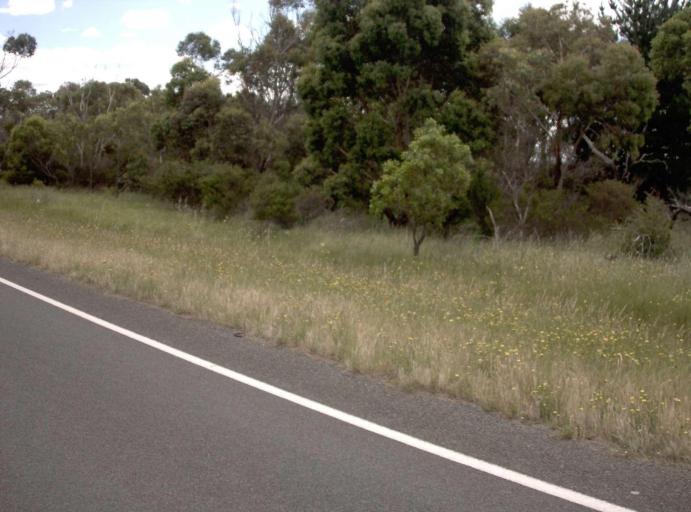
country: AU
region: Victoria
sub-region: Cardinia
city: Koo-Wee-Rup
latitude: -38.3135
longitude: 145.5404
